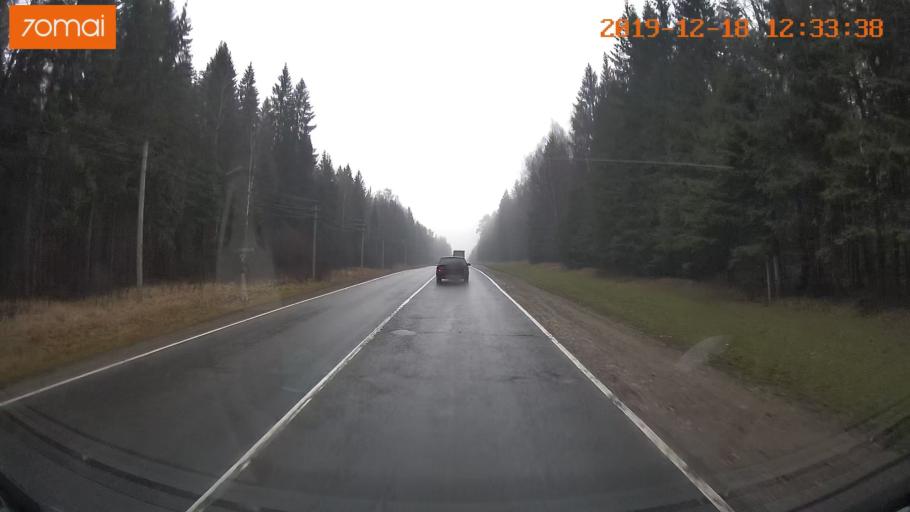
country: RU
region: Moskovskaya
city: Rumyantsevo
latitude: 56.1144
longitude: 36.5631
